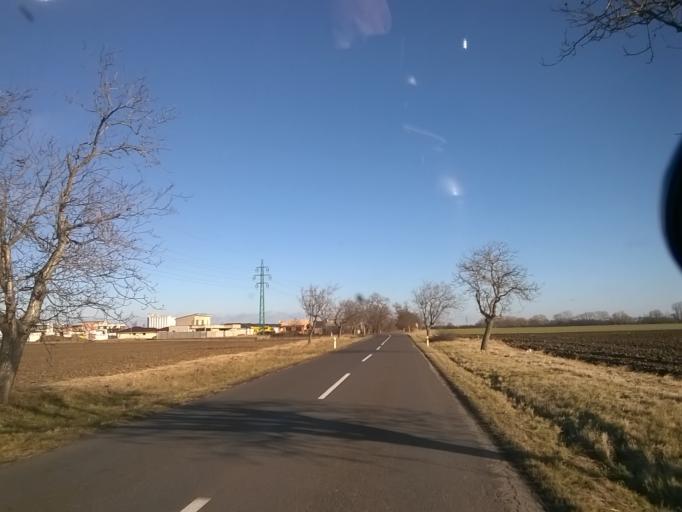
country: SK
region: Bratislavsky
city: Senec
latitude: 48.2022
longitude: 17.3919
